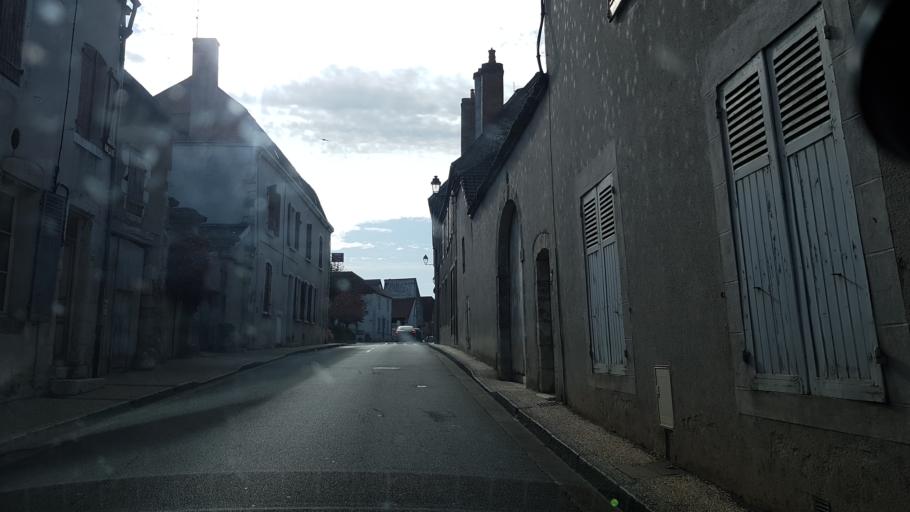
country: FR
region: Centre
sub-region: Departement du Loiret
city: Bonny-sur-Loire
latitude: 47.5606
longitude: 2.8390
